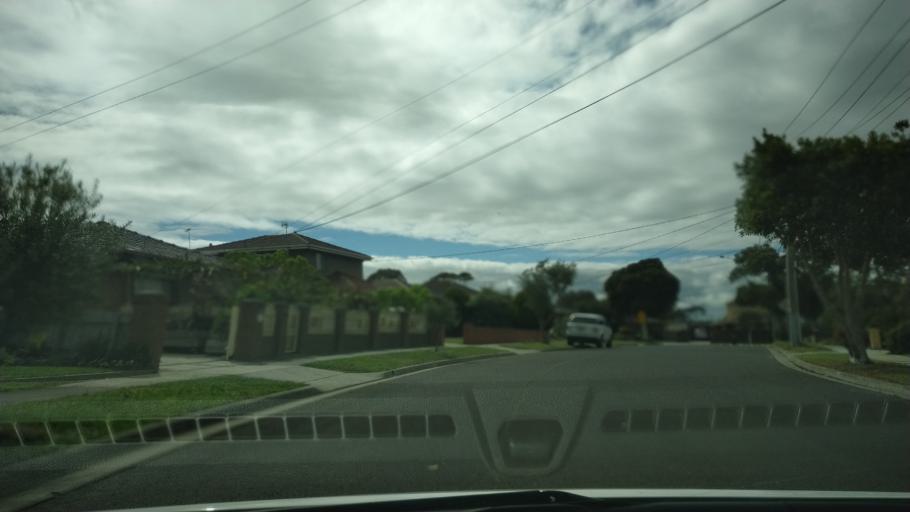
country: AU
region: Victoria
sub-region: Greater Dandenong
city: Keysborough
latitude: -37.9855
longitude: 145.1724
